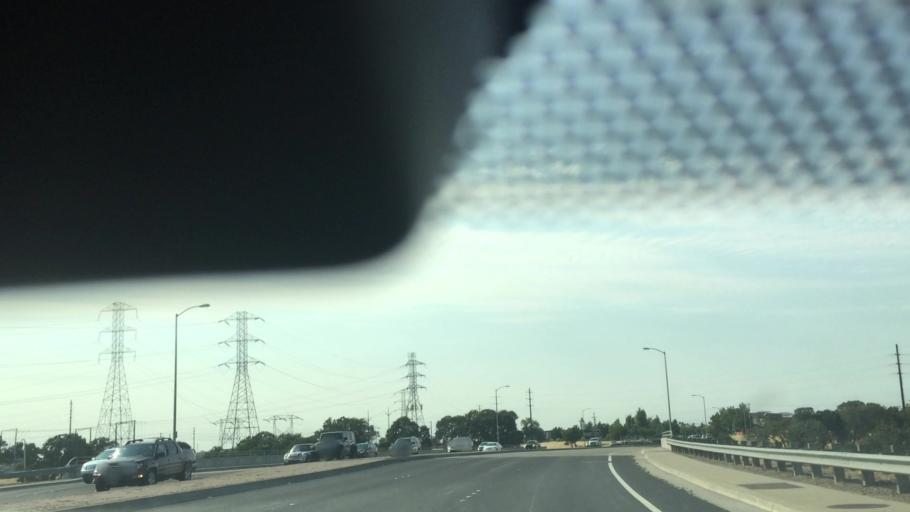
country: US
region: California
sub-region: Placer County
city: Roseville
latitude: 38.7637
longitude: -121.2598
